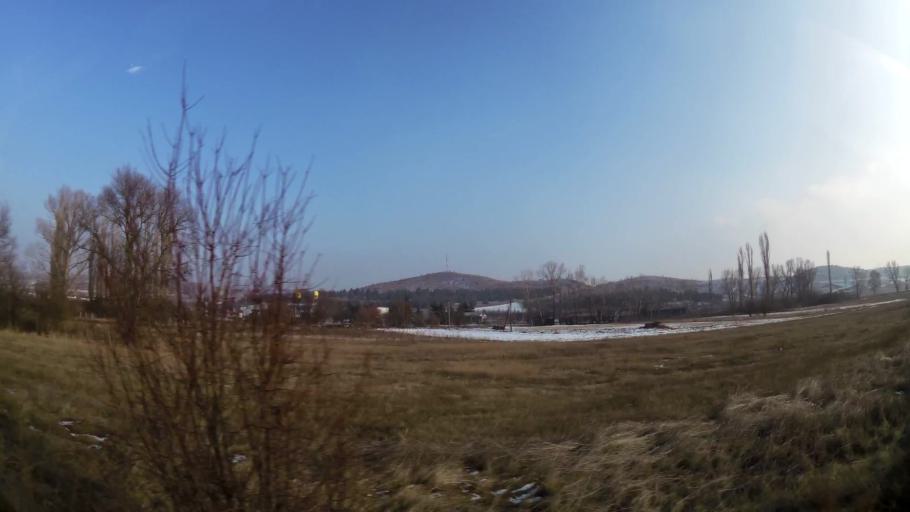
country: MK
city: Miladinovci
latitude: 41.9955
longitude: 21.6567
